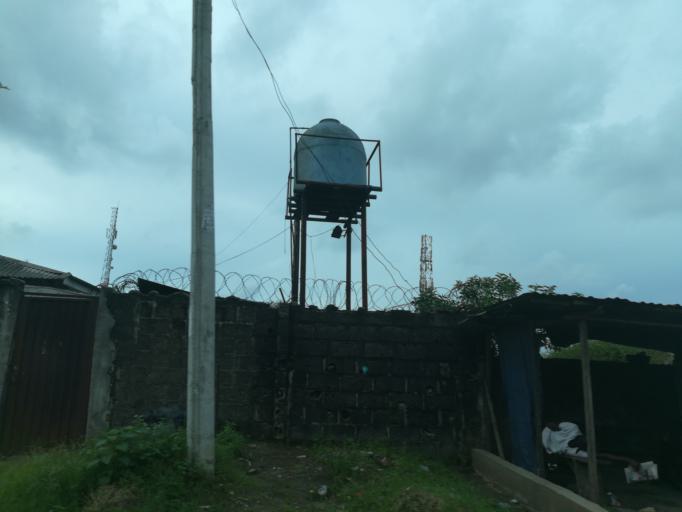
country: NG
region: Rivers
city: Port Harcourt
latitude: 4.8129
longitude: 6.9883
